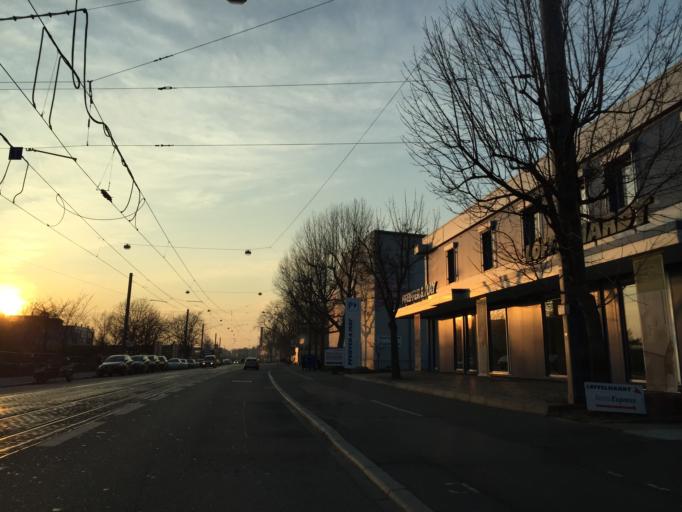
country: DE
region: Baden-Wuerttemberg
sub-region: Karlsruhe Region
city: Eppelheim
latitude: 49.4057
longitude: 8.6633
